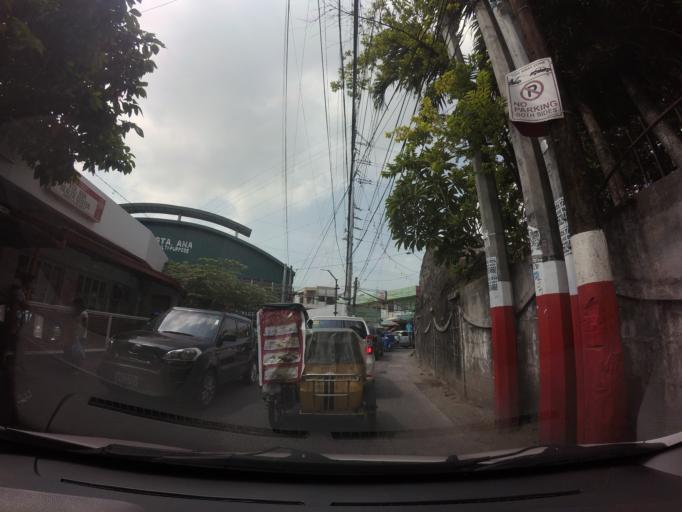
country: PH
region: Calabarzon
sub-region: Province of Rizal
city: Taguig
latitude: 14.5267
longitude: 121.0746
